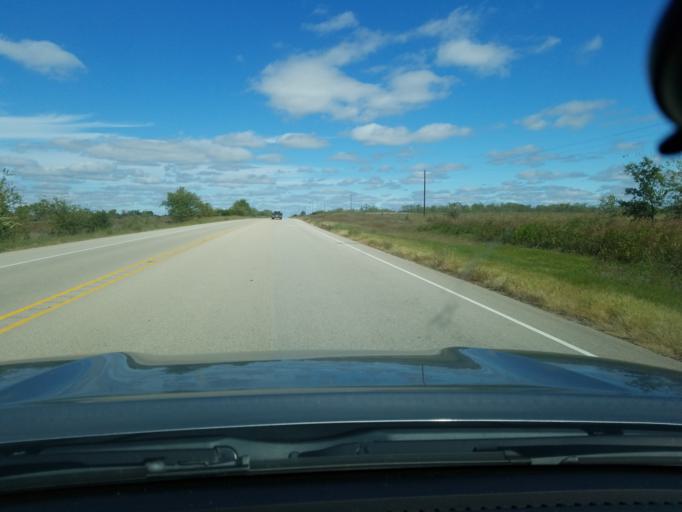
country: US
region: Texas
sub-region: Hamilton County
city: Hamilton
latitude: 31.6583
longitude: -98.1431
